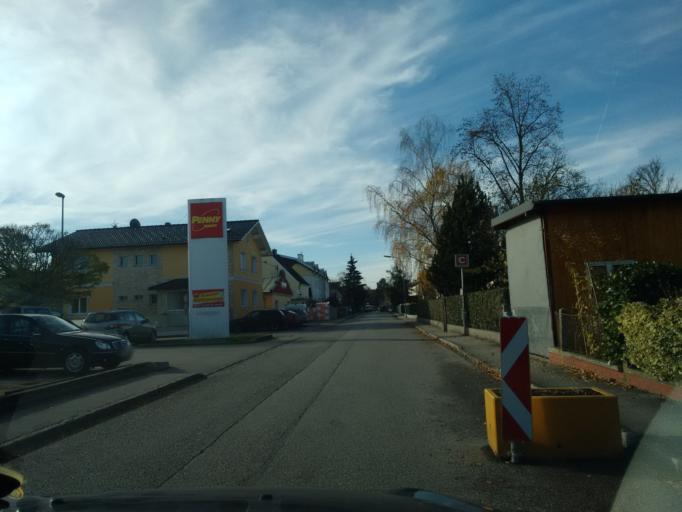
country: AT
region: Upper Austria
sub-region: Politischer Bezirk Linz-Land
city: Traun
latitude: 48.2421
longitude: 14.2584
